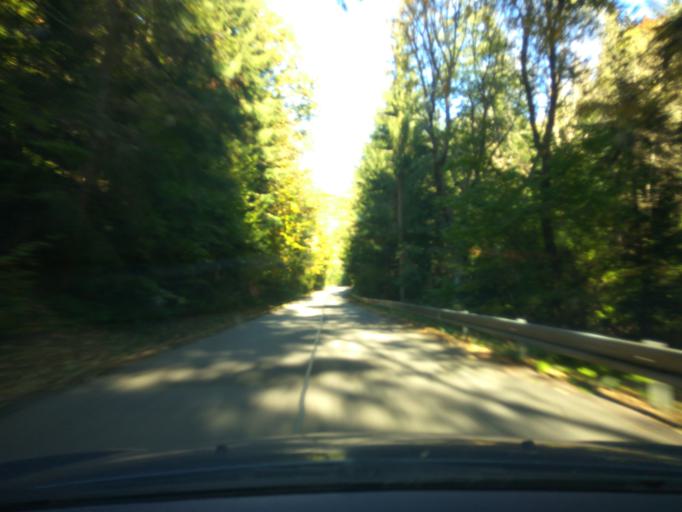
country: SK
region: Banskobystricky
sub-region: Okres Ziar nad Hronom
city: Kremnica
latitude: 48.7196
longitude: 18.9640
